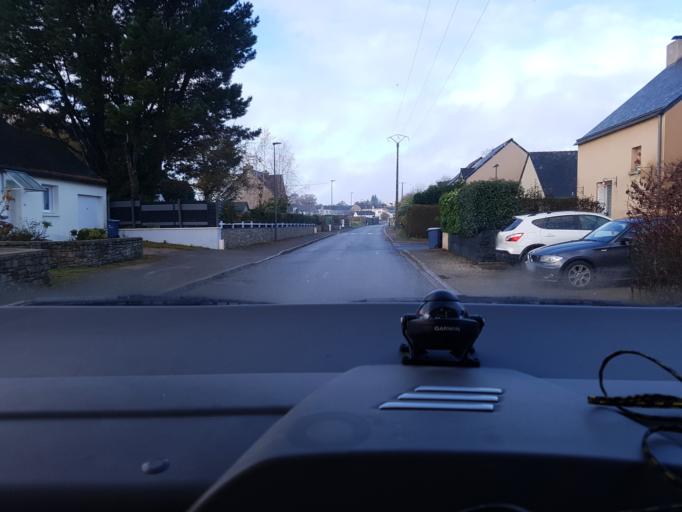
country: FR
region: Brittany
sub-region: Departement d'Ille-et-Vilaine
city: La Bouexiere
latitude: 48.1844
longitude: -1.4309
